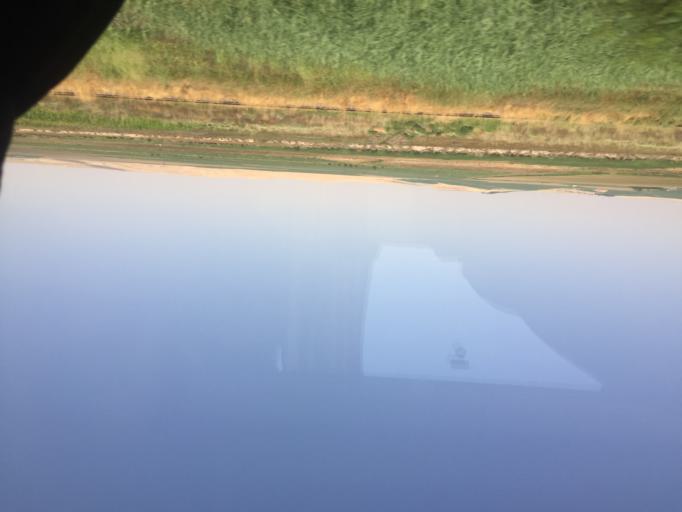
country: TR
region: Diyarbakir
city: Tepe
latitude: 37.8497
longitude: 40.7873
